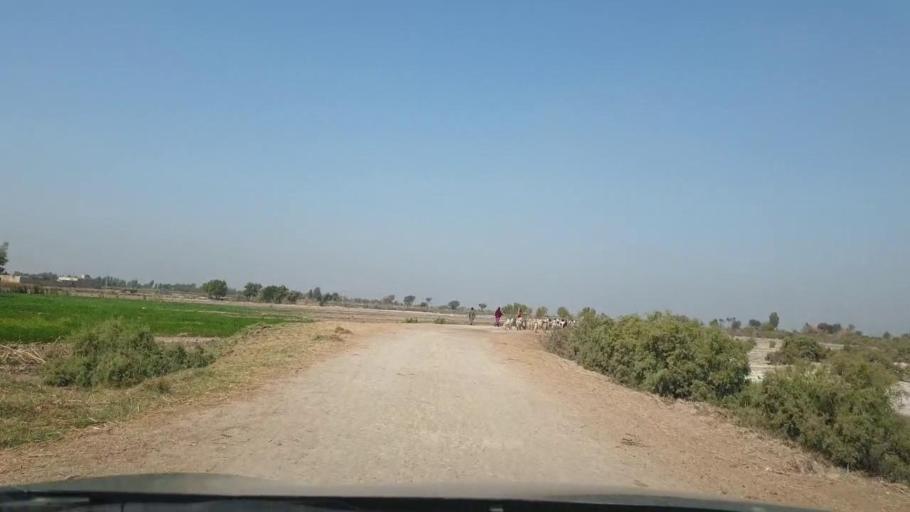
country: PK
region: Sindh
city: Berani
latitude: 25.6831
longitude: 68.8910
